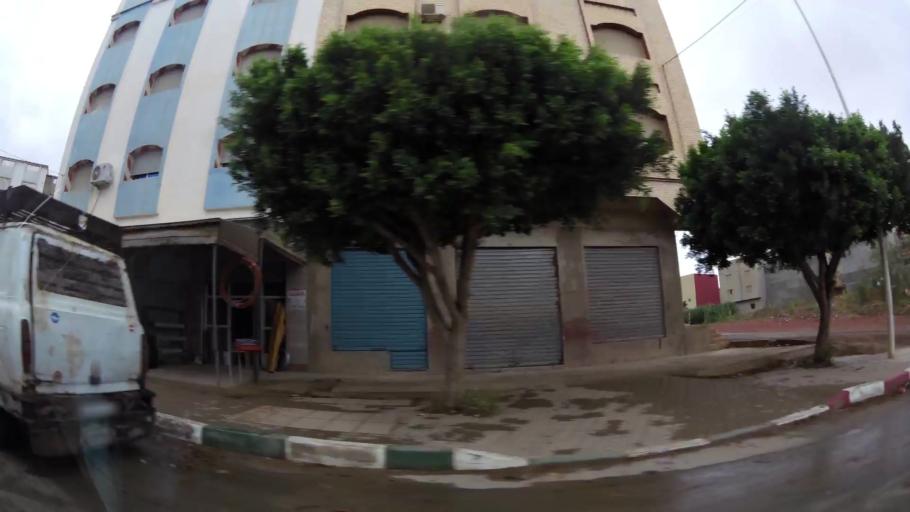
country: MA
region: Oriental
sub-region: Nador
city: Midar
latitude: 35.0492
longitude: -3.4587
